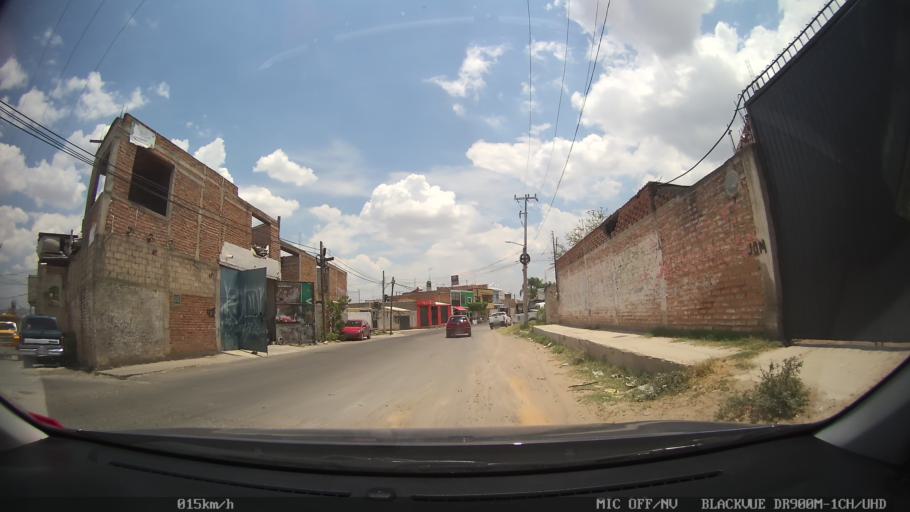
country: MX
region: Jalisco
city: Tonala
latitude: 20.6249
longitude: -103.2290
